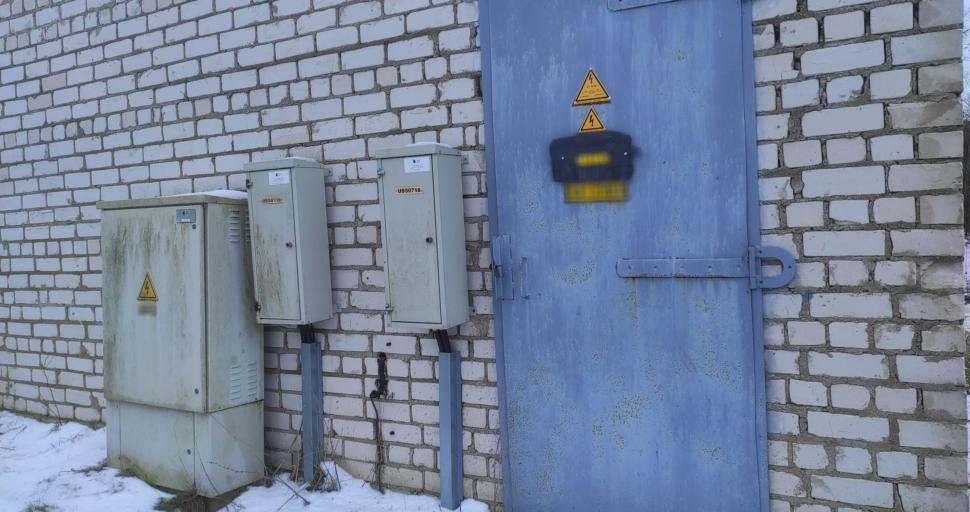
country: LV
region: Dundaga
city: Dundaga
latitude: 57.3669
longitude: 22.0604
